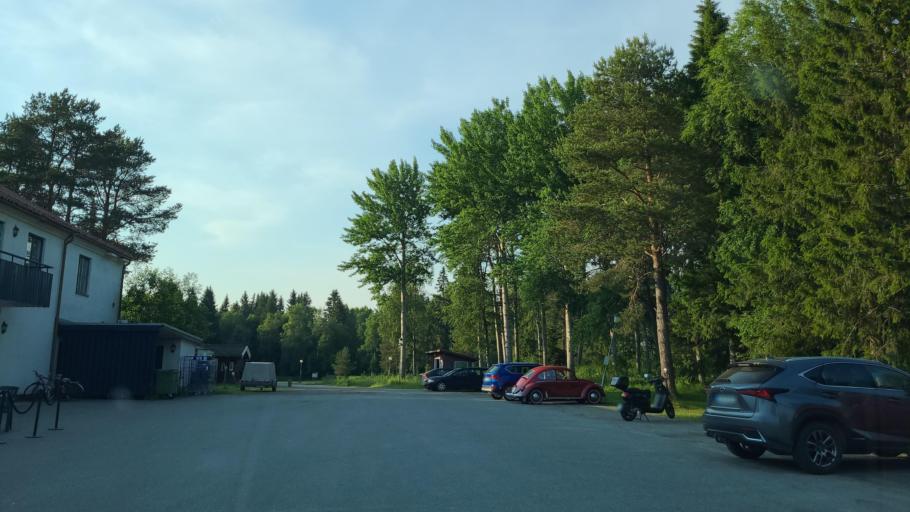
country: SE
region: Vaesterbotten
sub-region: Skelleftea Kommun
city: Burea
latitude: 64.3699
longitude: 21.3195
